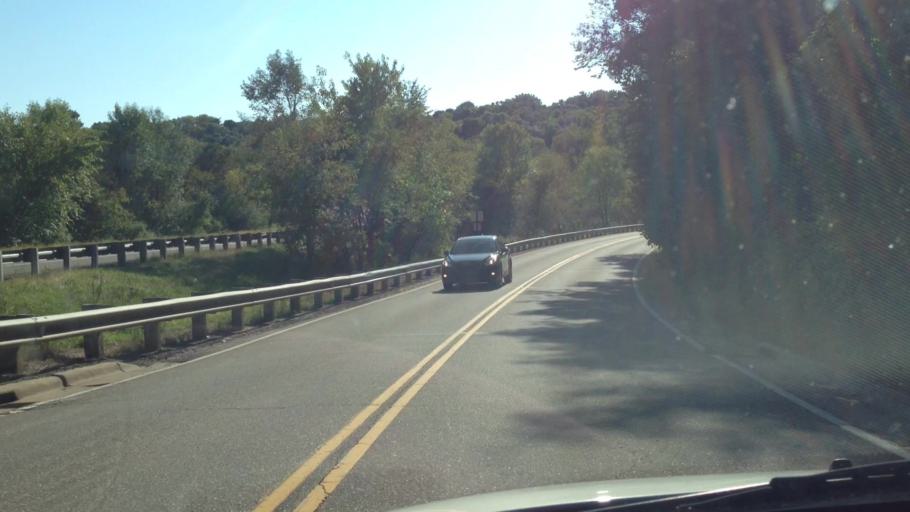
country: US
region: Minnesota
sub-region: Washington County
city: Stillwater
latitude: 45.0773
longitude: -92.8056
